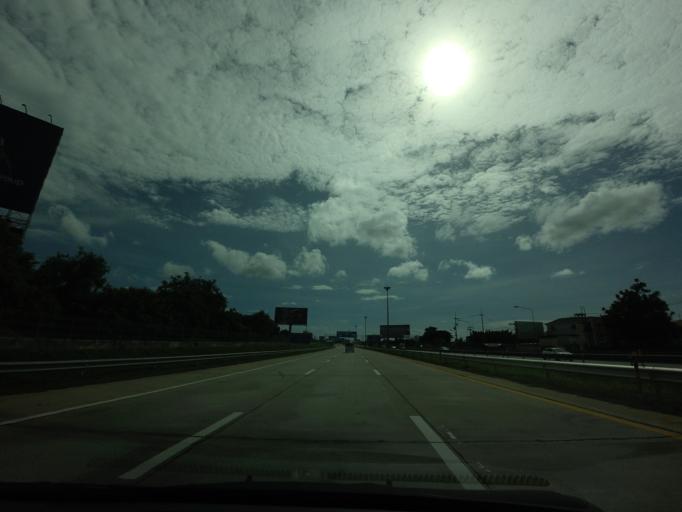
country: TH
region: Chon Buri
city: Phatthaya
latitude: 12.9507
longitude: 100.9462
